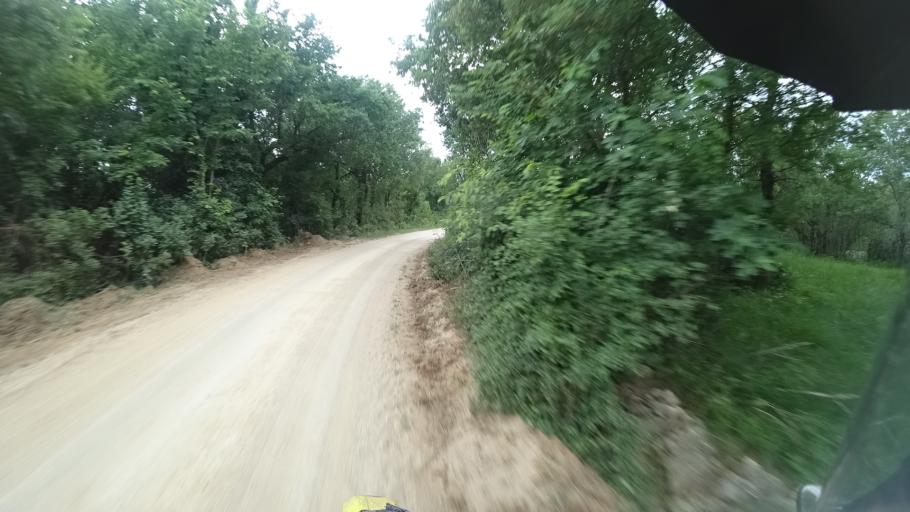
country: HR
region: Sibensko-Kniniska
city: Kistanje
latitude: 44.1072
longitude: 15.9453
